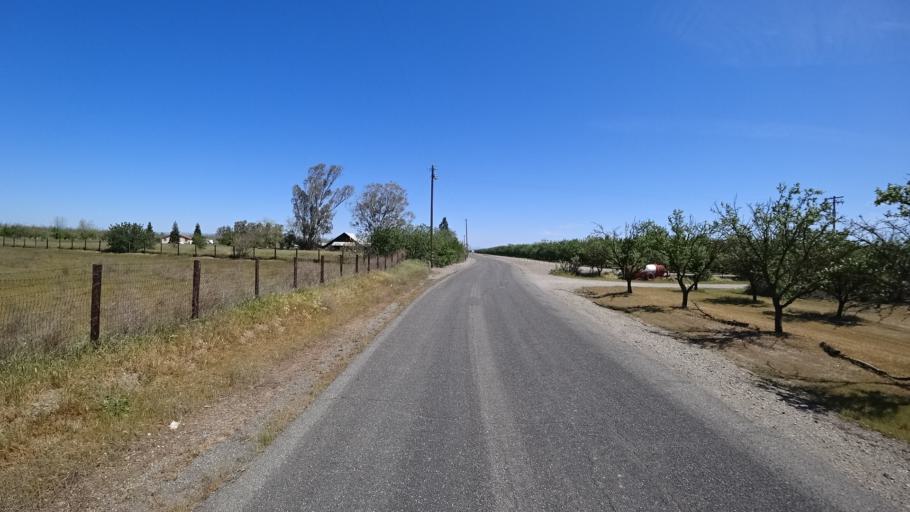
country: US
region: California
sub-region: Glenn County
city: Orland
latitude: 39.7325
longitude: -122.1506
